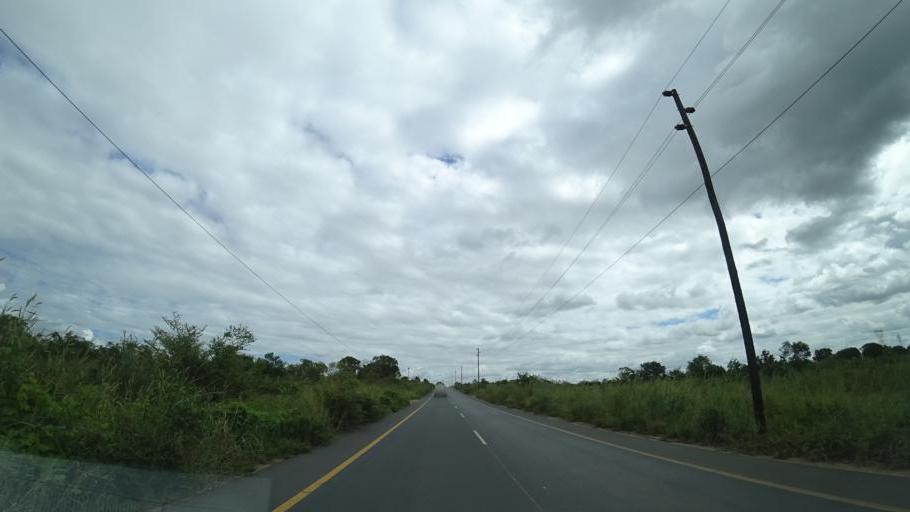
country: MZ
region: Sofala
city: Dondo
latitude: -19.5065
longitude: 34.6060
